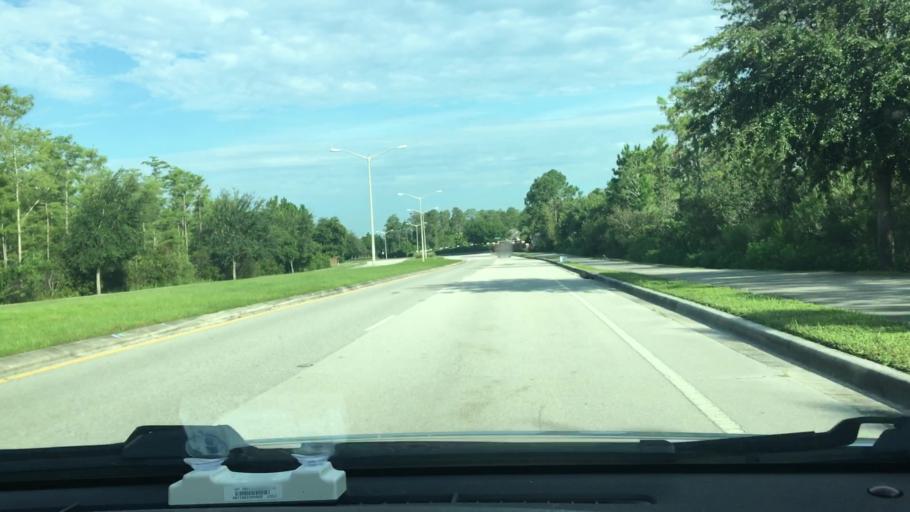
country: US
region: Florida
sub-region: Orange County
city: Conway
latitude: 28.4333
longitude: -81.2440
